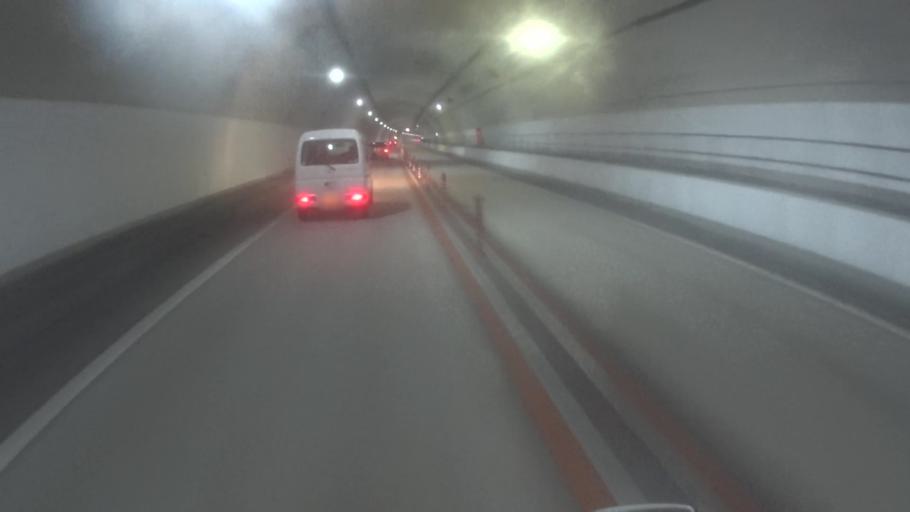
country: JP
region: Kyoto
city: Ayabe
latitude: 35.3085
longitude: 135.3266
